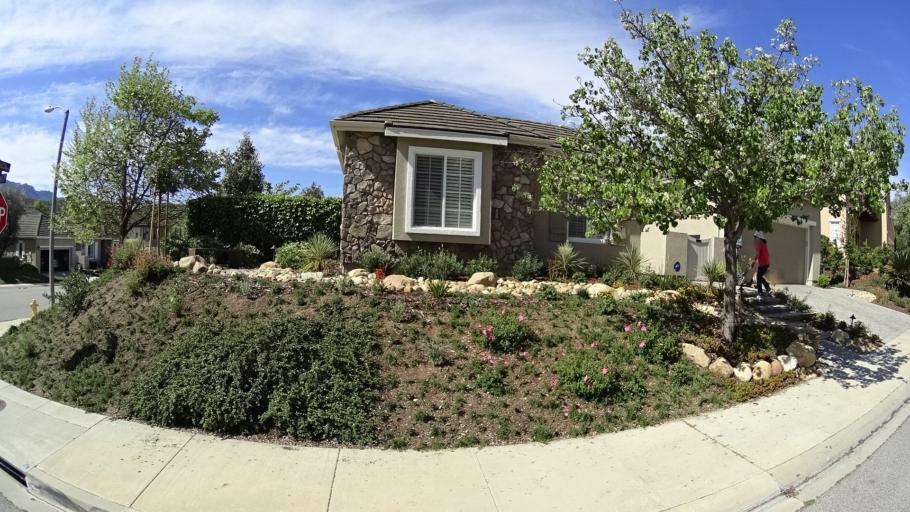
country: US
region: California
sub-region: Ventura County
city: Casa Conejo
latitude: 34.1737
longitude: -118.9696
